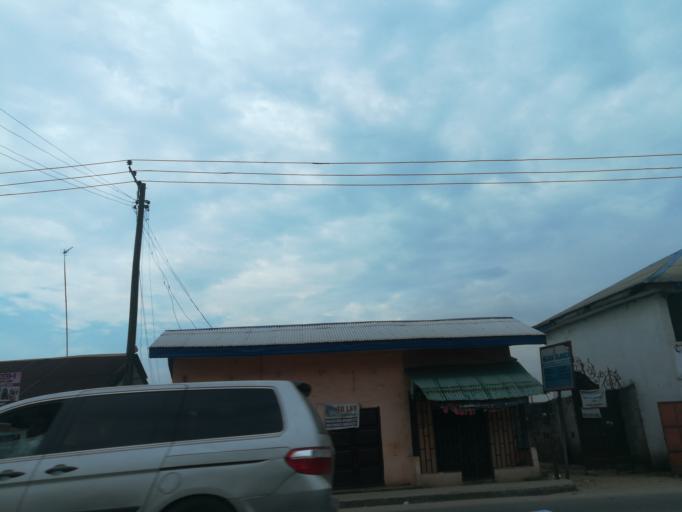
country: NG
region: Rivers
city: Port Harcourt
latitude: 4.8500
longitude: 6.9783
